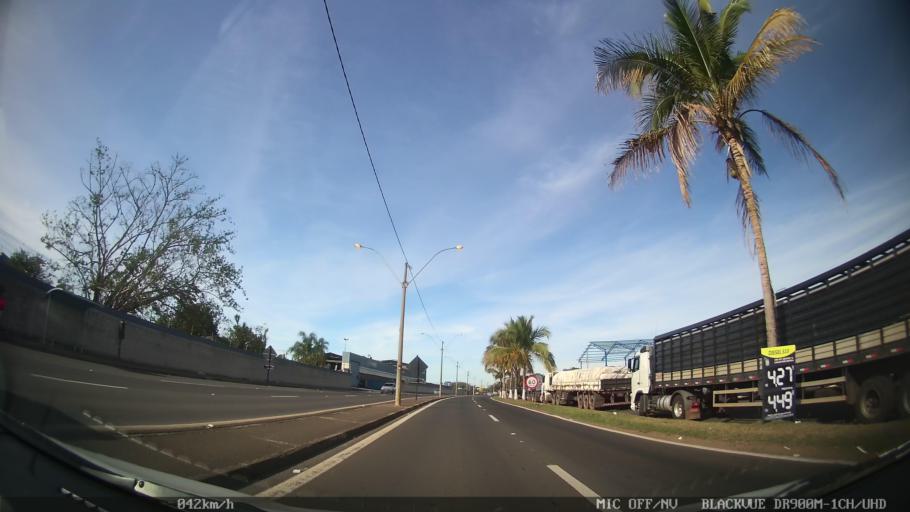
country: BR
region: Sao Paulo
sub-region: Piracicaba
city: Piracicaba
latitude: -22.7599
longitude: -47.6453
